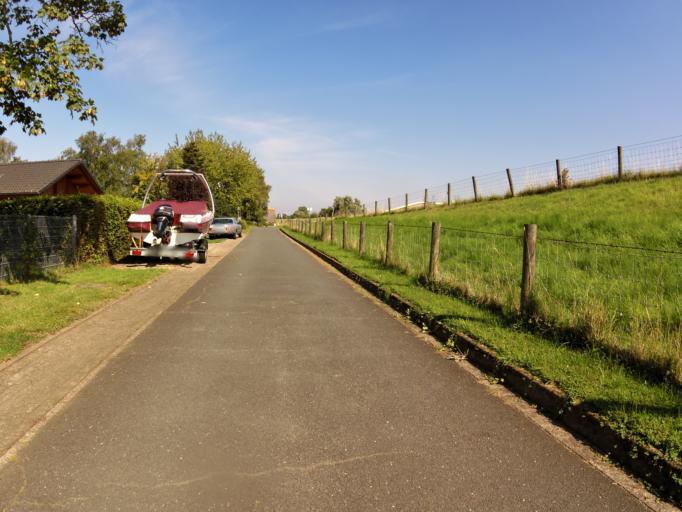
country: DE
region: Lower Saxony
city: Elsfleth
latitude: 53.2671
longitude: 8.4798
